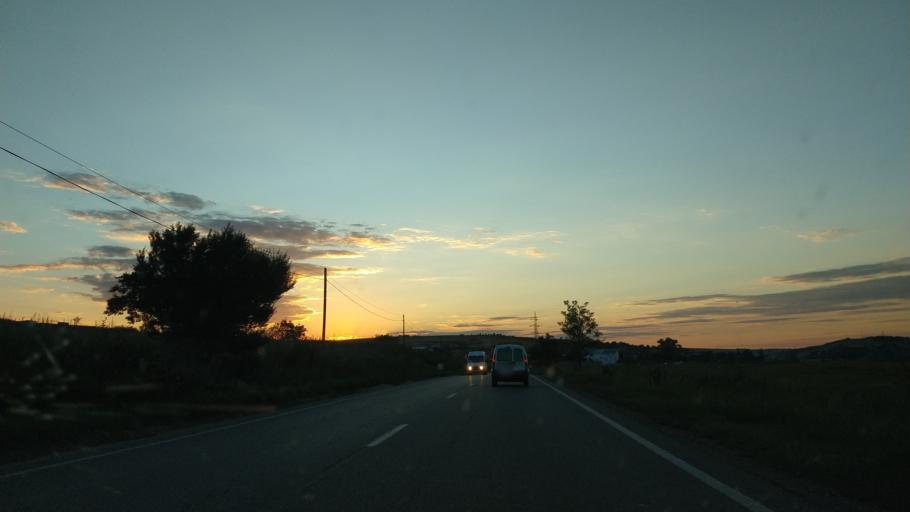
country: RO
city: Vanatori
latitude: 47.2264
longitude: 27.5407
